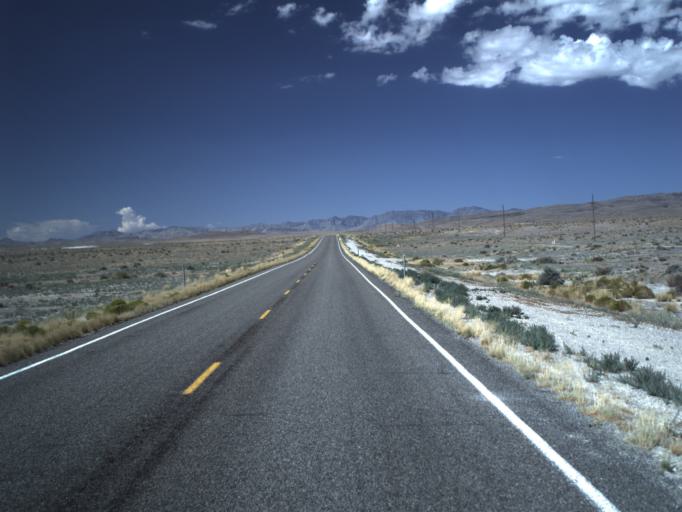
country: US
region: Utah
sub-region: Millard County
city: Delta
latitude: 39.0815
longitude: -113.1948
